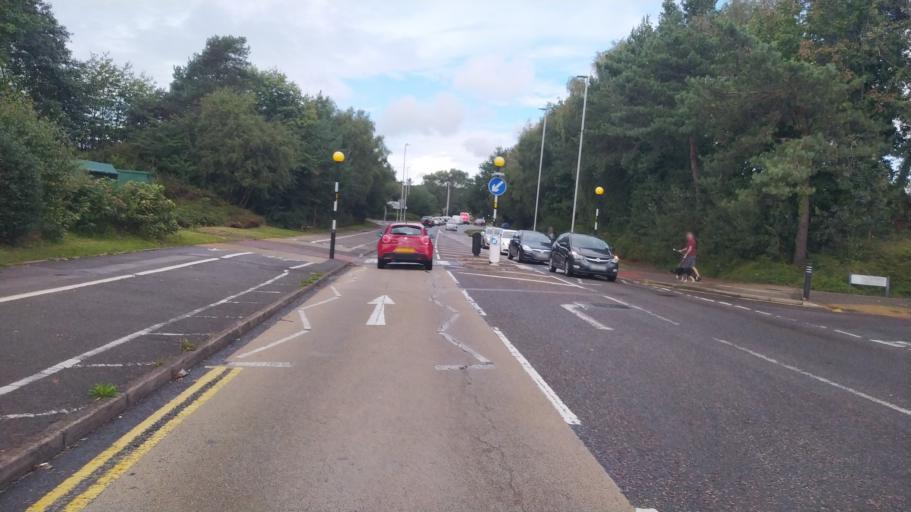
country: GB
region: England
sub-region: Poole
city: Canford Heath
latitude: 50.7488
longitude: -1.9653
